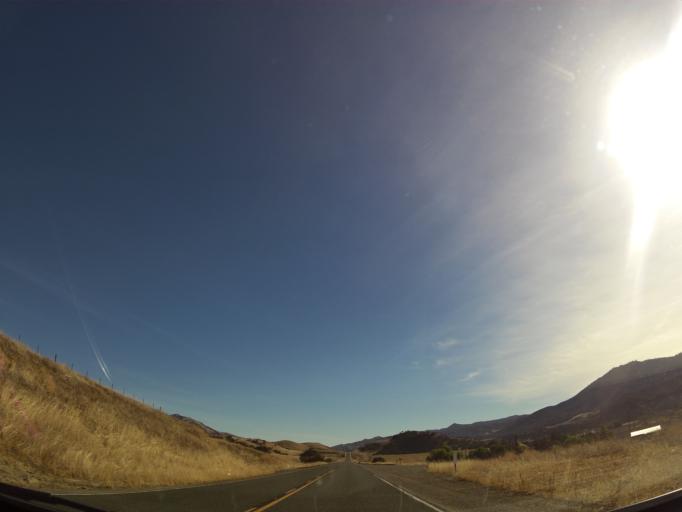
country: US
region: California
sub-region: San Benito County
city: Ridgemark
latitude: 36.6626
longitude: -121.2463
